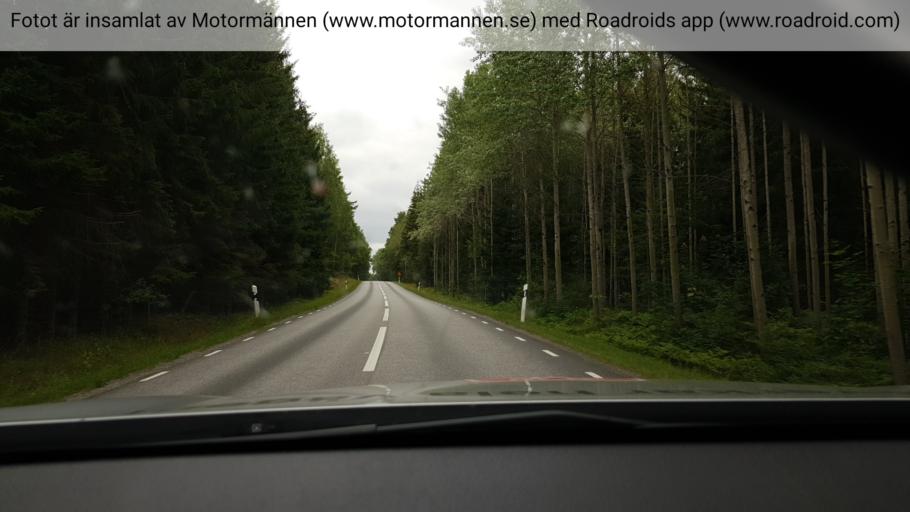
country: SE
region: Stockholm
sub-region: Norrtalje Kommun
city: Skanninge
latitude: 59.8837
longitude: 18.4872
